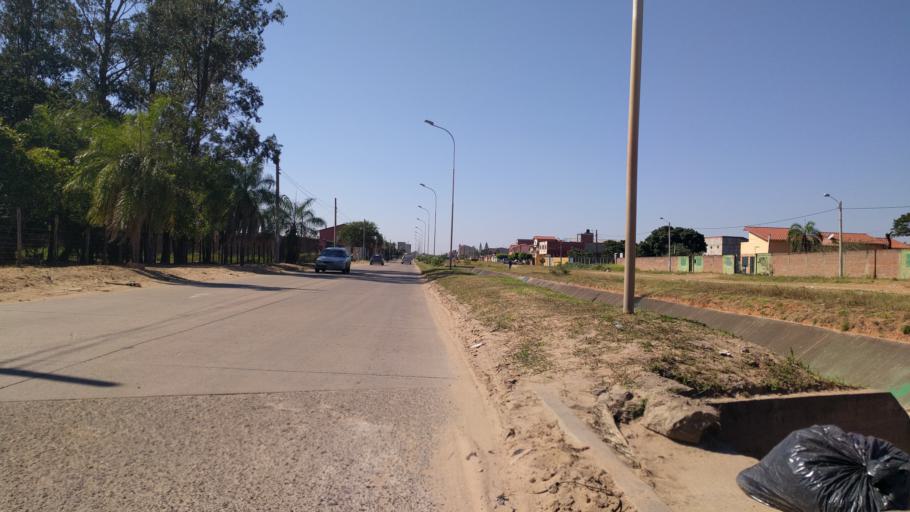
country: BO
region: Santa Cruz
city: Santa Cruz de la Sierra
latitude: -17.8430
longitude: -63.1892
